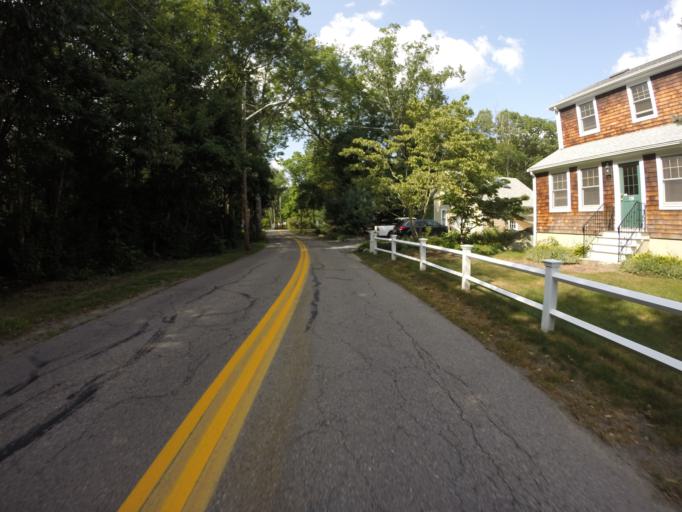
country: US
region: Massachusetts
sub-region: Norfolk County
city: Stoughton
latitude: 42.0813
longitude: -71.1121
